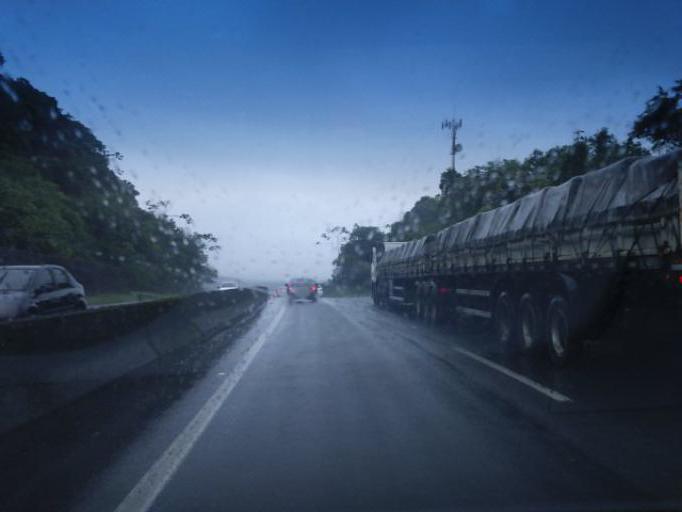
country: BR
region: Santa Catarina
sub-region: Joinville
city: Joinville
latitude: -26.0871
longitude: -48.8622
